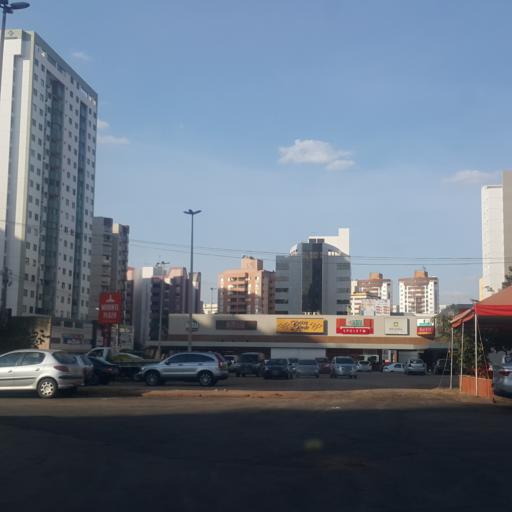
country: BR
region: Federal District
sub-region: Brasilia
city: Brasilia
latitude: -15.8385
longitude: -48.0162
